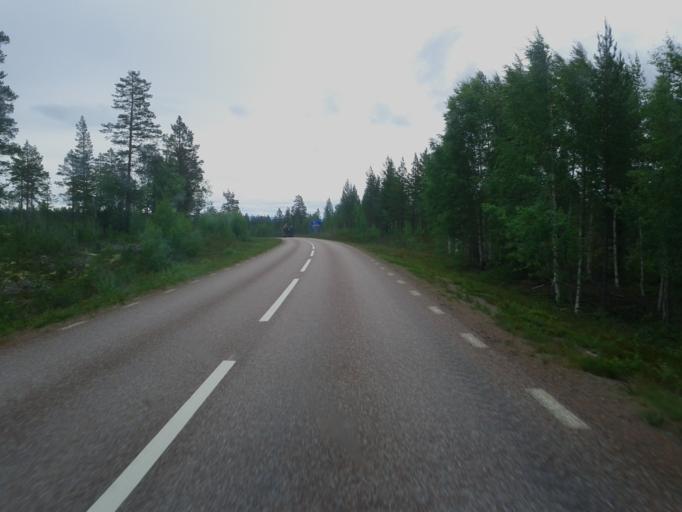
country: NO
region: Hedmark
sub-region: Trysil
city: Innbygda
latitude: 61.6924
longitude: 13.0639
